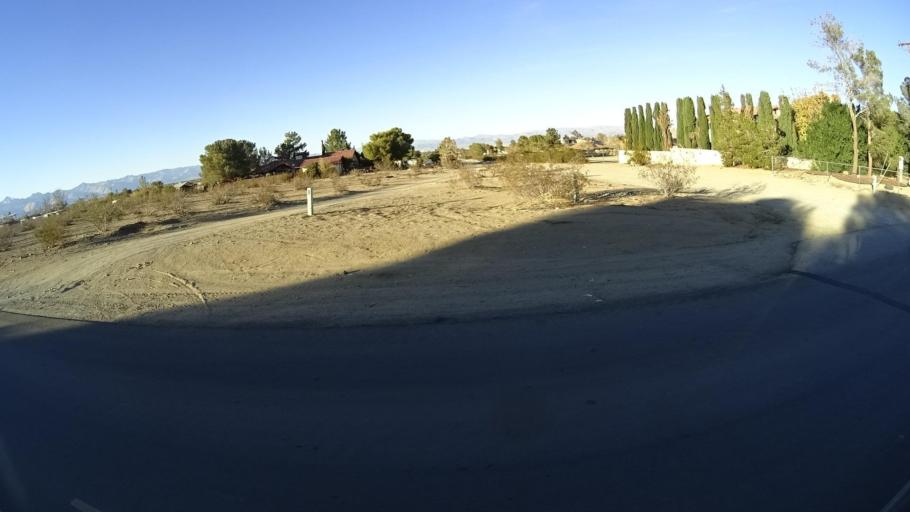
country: US
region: California
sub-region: Kern County
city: Ridgecrest
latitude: 35.5860
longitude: -117.6580
